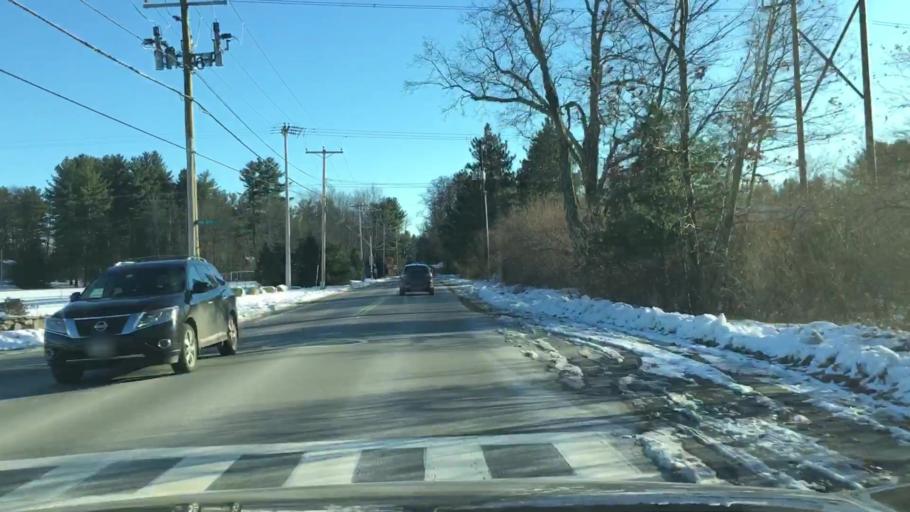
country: US
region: New Hampshire
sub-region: Hillsborough County
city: Milford
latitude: 42.8239
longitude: -71.5826
